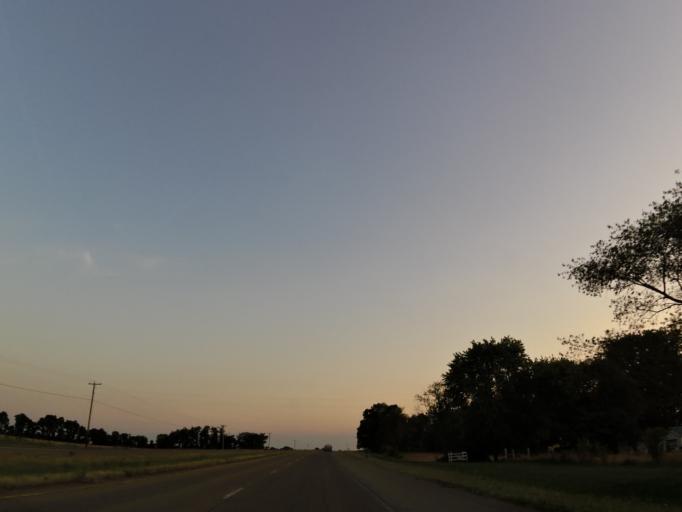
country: US
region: Tennessee
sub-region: Carroll County
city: McKenzie
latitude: 36.1724
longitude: -88.4472
